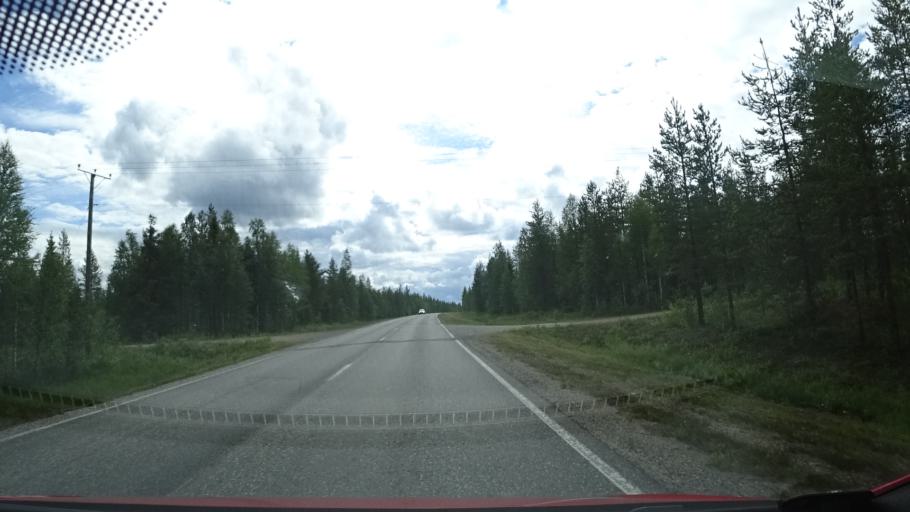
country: FI
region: Lapland
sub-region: Tunturi-Lappi
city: Kittilae
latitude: 67.5265
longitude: 24.9080
